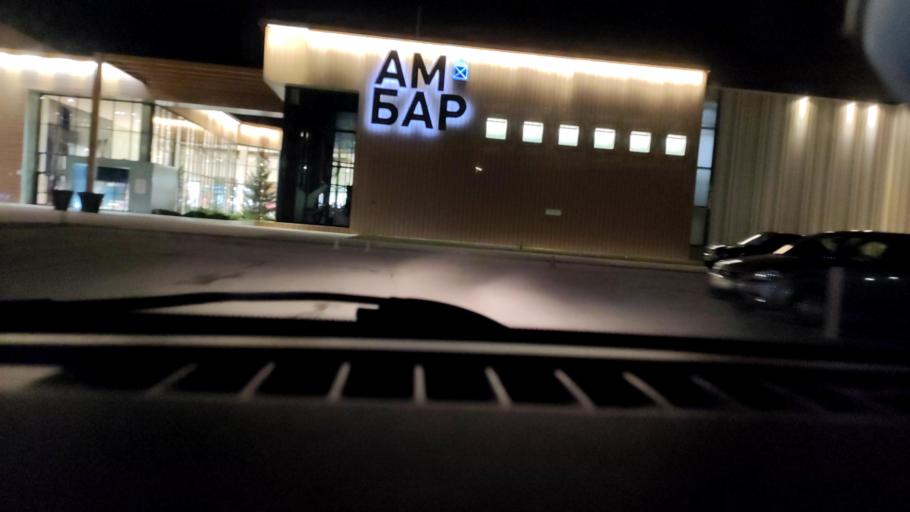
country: RU
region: Samara
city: Samara
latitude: 53.1409
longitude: 50.1721
